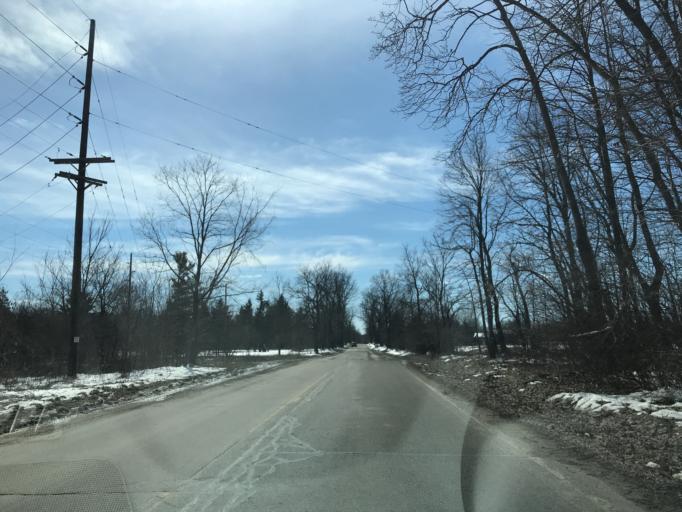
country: US
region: Michigan
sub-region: Livingston County
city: Whitmore Lake
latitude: 42.4371
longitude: -83.7249
